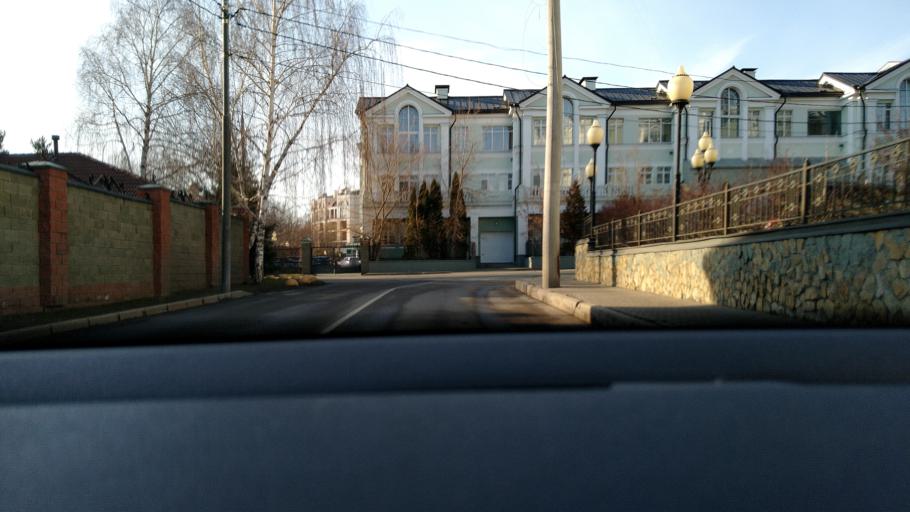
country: RU
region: Moskovskaya
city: Levoberezhnyy
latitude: 55.8314
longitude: 37.4701
